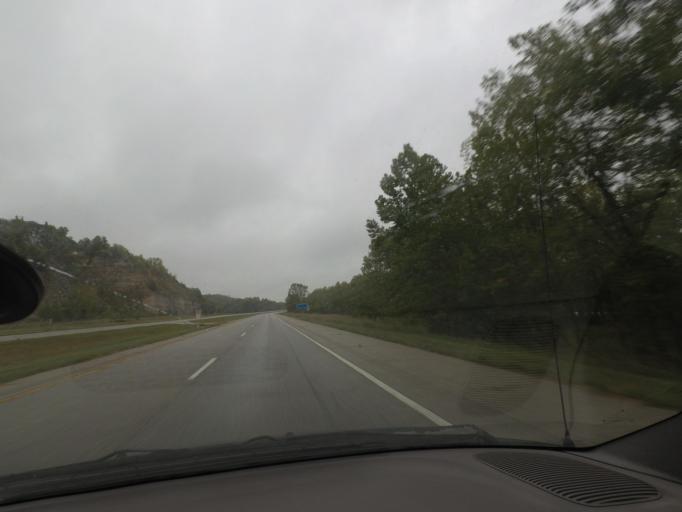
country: US
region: Illinois
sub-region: Pike County
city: Barry
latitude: 39.7152
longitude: -91.0760
